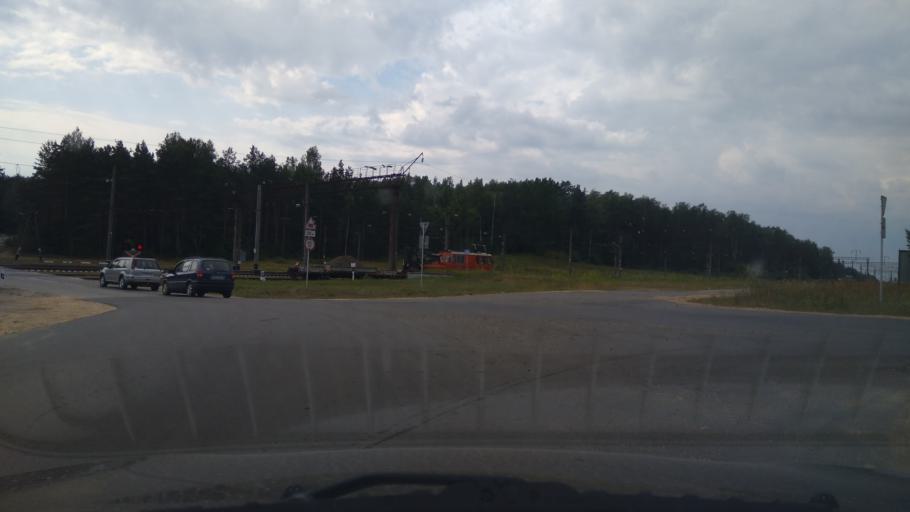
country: BY
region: Brest
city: Nyakhachava
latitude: 52.6050
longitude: 25.0854
